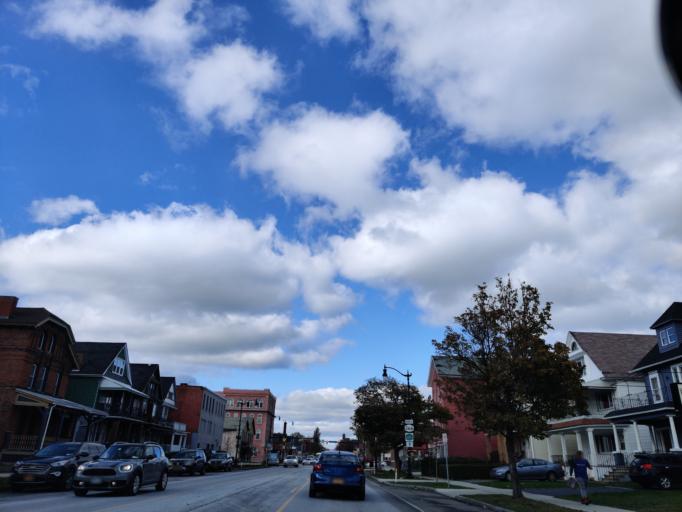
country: US
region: New York
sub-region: Erie County
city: Buffalo
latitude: 42.8972
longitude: -78.8883
